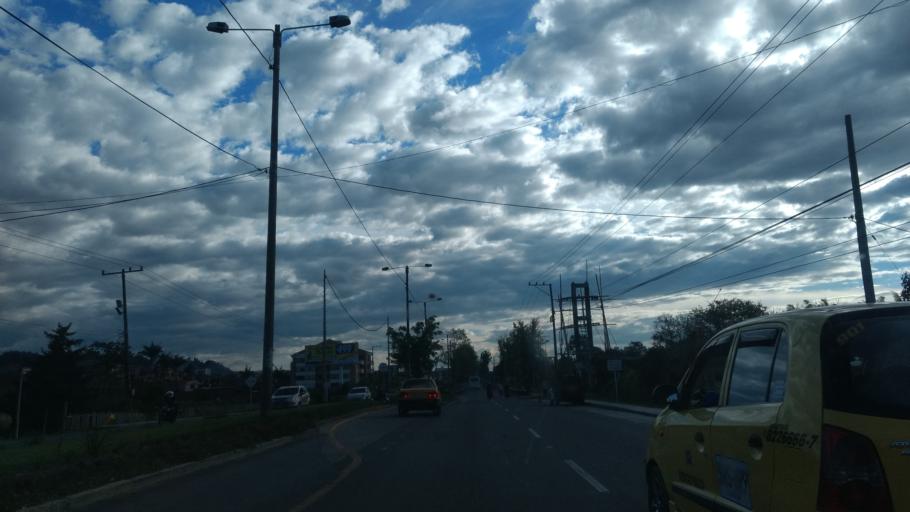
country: CO
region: Cauca
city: Popayan
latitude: 2.4642
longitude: -76.5890
